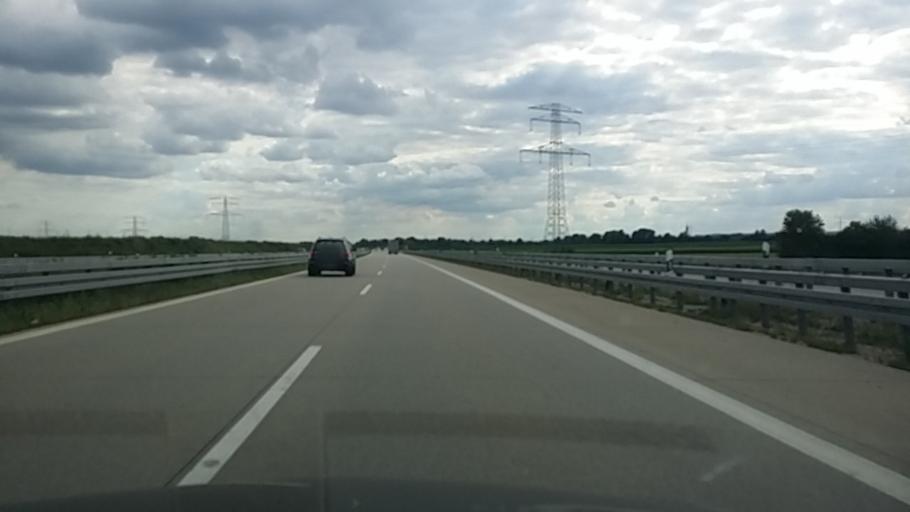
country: DE
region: Bavaria
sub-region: Lower Bavaria
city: Essenbach
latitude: 48.6005
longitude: 12.2297
